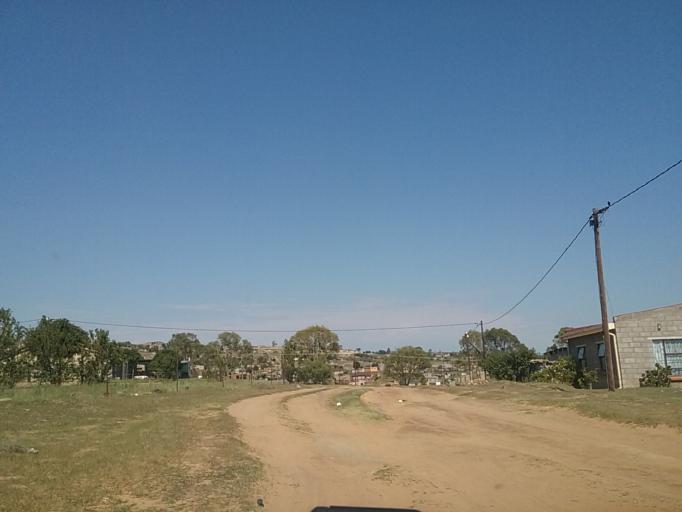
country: LS
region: Berea
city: Teyateyaneng
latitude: -29.1305
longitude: 27.7594
